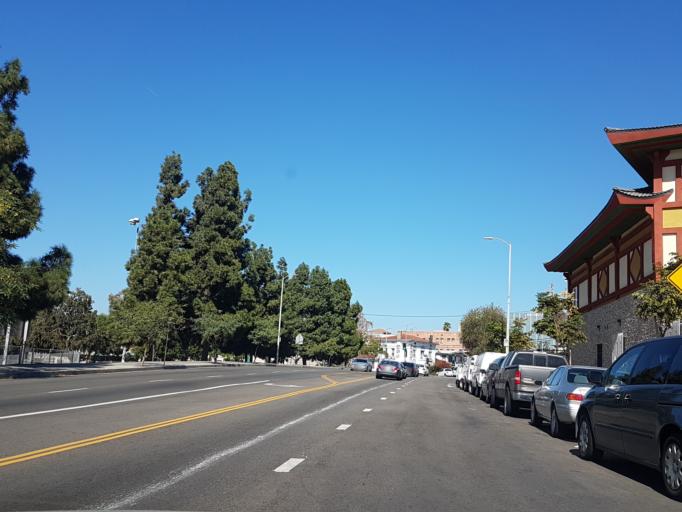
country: US
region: California
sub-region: Los Angeles County
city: Silver Lake
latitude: 34.0533
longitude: -118.3003
